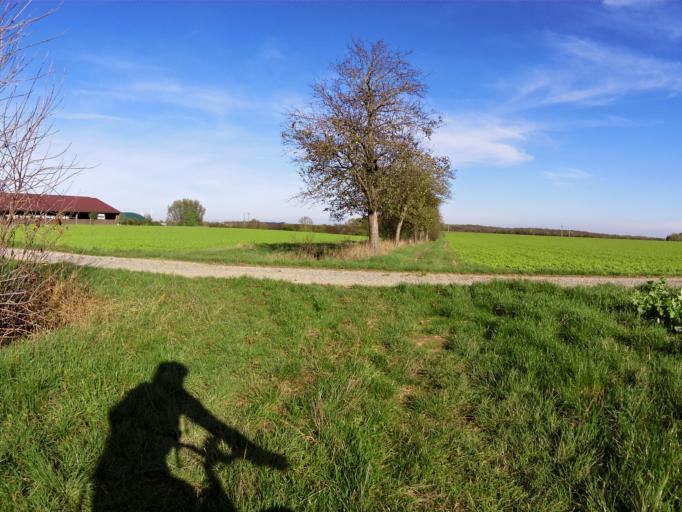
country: DE
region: Bavaria
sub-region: Regierungsbezirk Unterfranken
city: Biebelried
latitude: 49.7247
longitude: 10.0901
